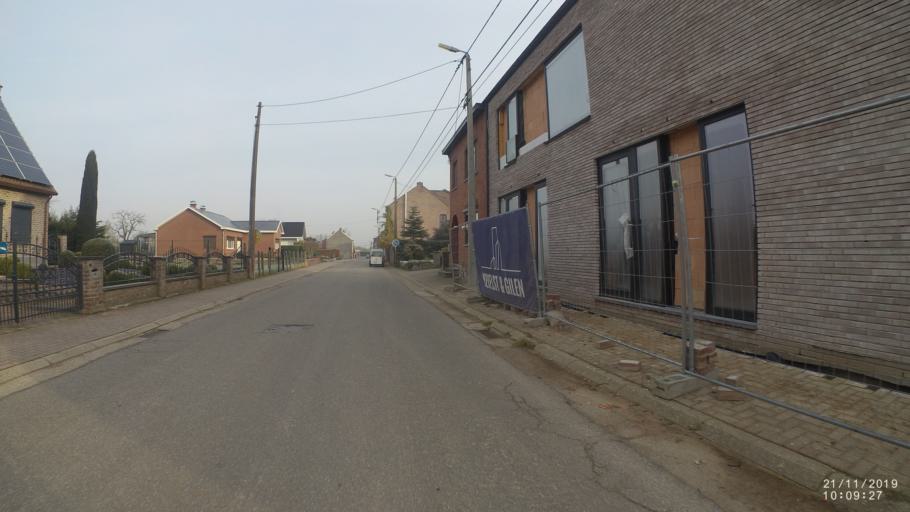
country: BE
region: Flanders
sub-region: Provincie Vlaams-Brabant
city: Zoutleeuw
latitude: 50.8101
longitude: 5.1099
